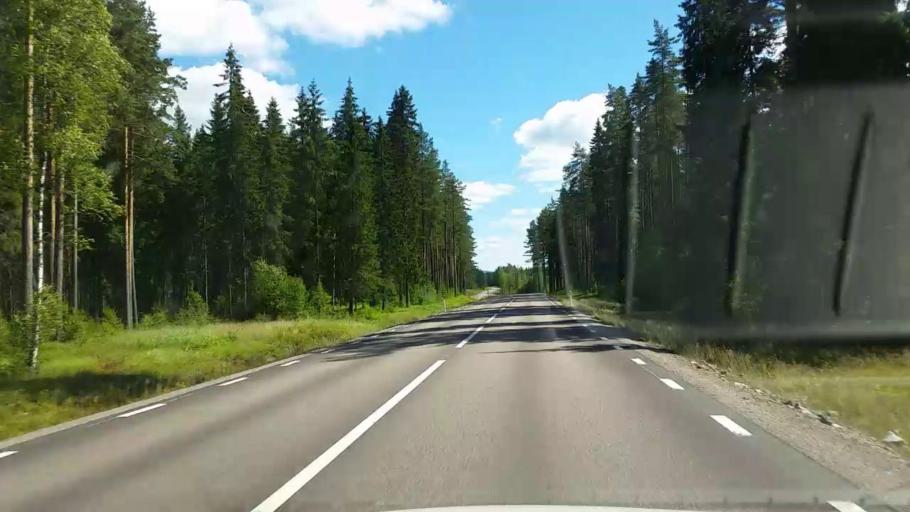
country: SE
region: Dalarna
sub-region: Faluns Kommun
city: Svardsjo
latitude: 60.7589
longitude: 15.7555
